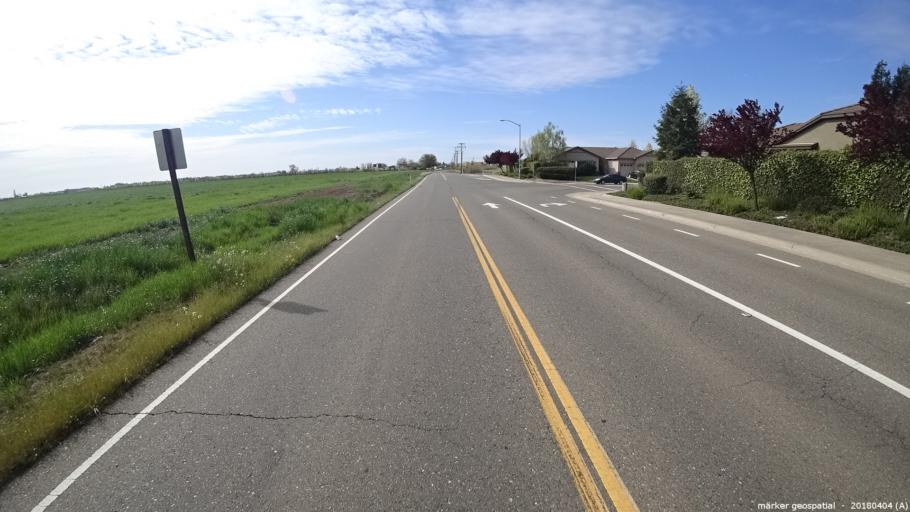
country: US
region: California
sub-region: Sacramento County
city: Galt
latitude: 38.2788
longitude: -121.2825
